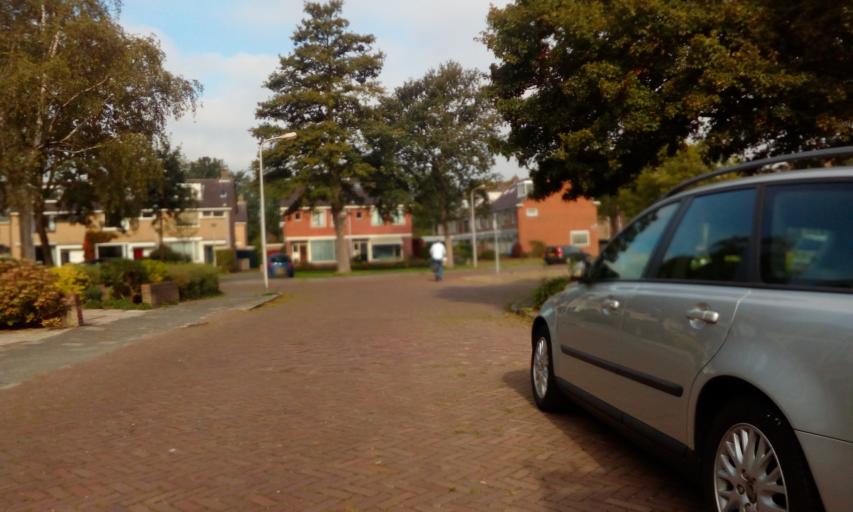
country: NL
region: South Holland
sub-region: Gemeente Voorschoten
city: Voorschoten
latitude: 52.1338
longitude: 4.4513
